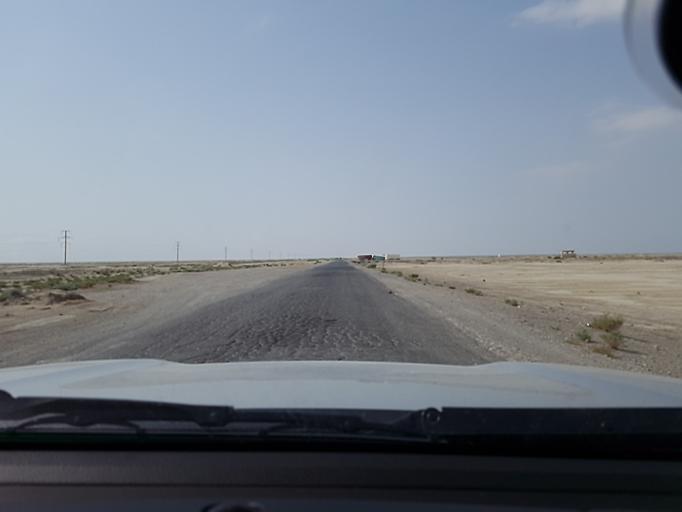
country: TM
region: Balkan
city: Gumdag
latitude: 38.9995
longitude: 54.5862
